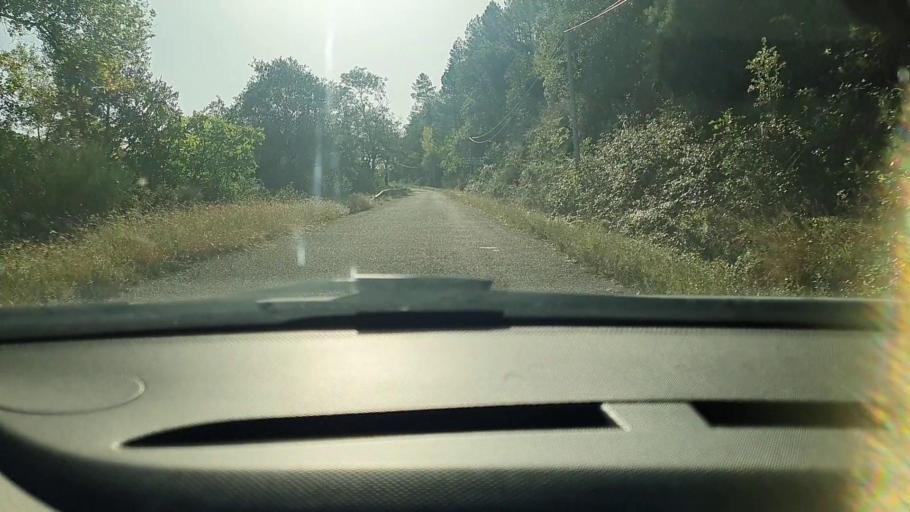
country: FR
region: Languedoc-Roussillon
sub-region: Departement du Gard
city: Besseges
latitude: 44.3177
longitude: 4.0485
